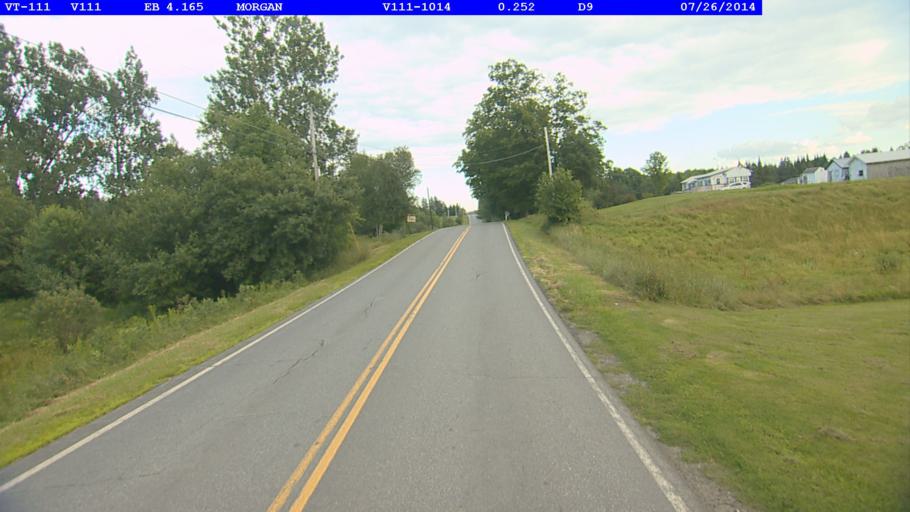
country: US
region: Vermont
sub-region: Orleans County
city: Newport
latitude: 44.9287
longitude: -72.0601
